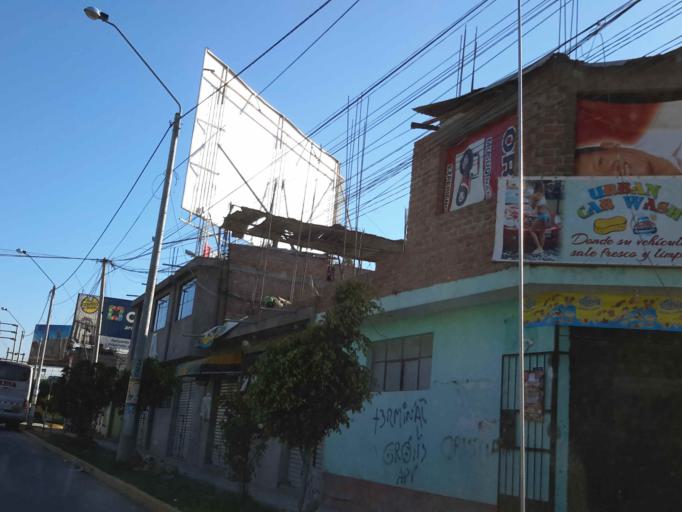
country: PE
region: Ayacucho
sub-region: Provincia de Huamanga
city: Ayacucho
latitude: -13.1356
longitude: -74.2292
